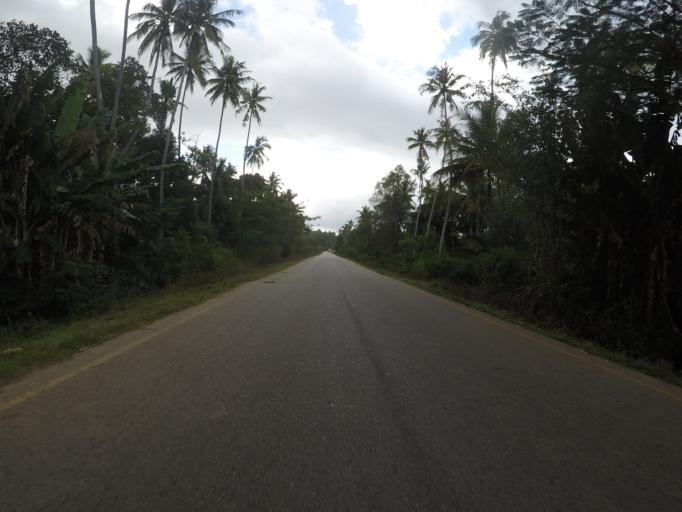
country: TZ
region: Zanzibar North
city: Mkokotoni
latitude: -5.9957
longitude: 39.1931
